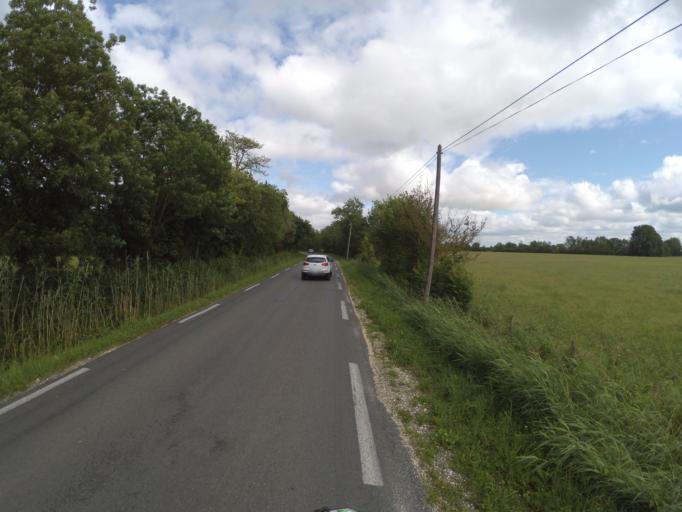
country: FR
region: Aquitaine
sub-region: Departement de la Gironde
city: Ludon-Medoc
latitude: 44.9889
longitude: -0.5808
